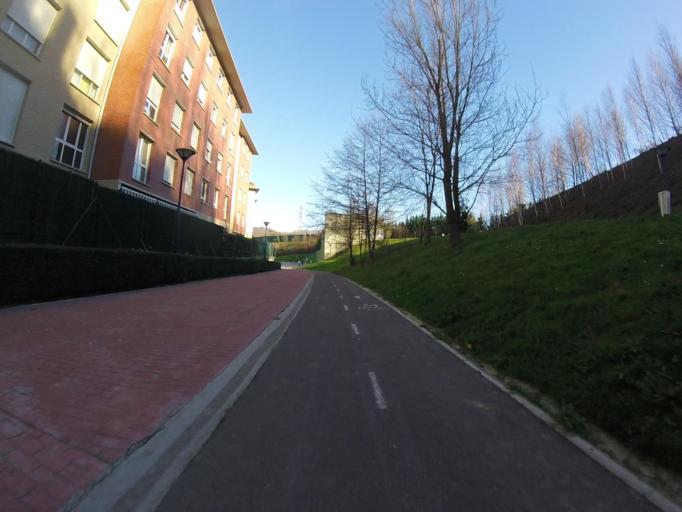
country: ES
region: Basque Country
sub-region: Provincia de Guipuzcoa
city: Errenteria
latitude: 43.3073
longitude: -1.8904
